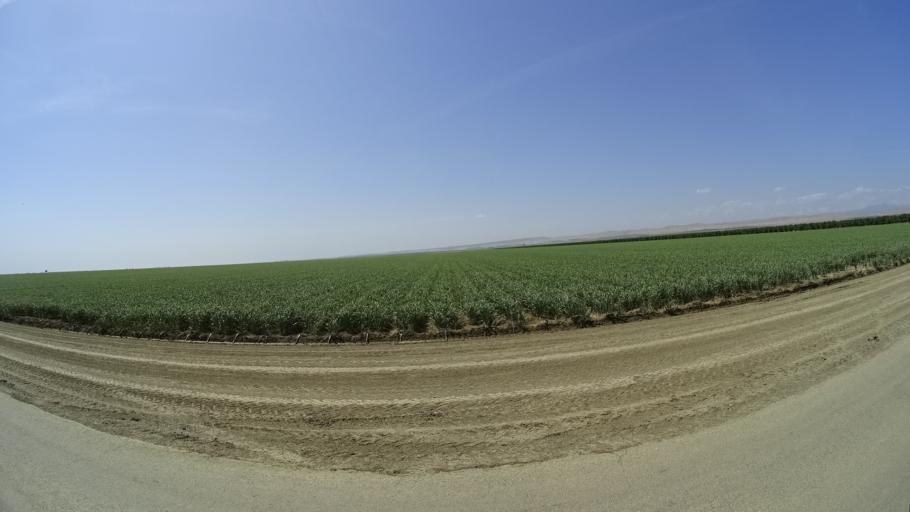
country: US
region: California
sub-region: Kings County
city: Kettleman City
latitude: 36.0943
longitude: -119.9839
